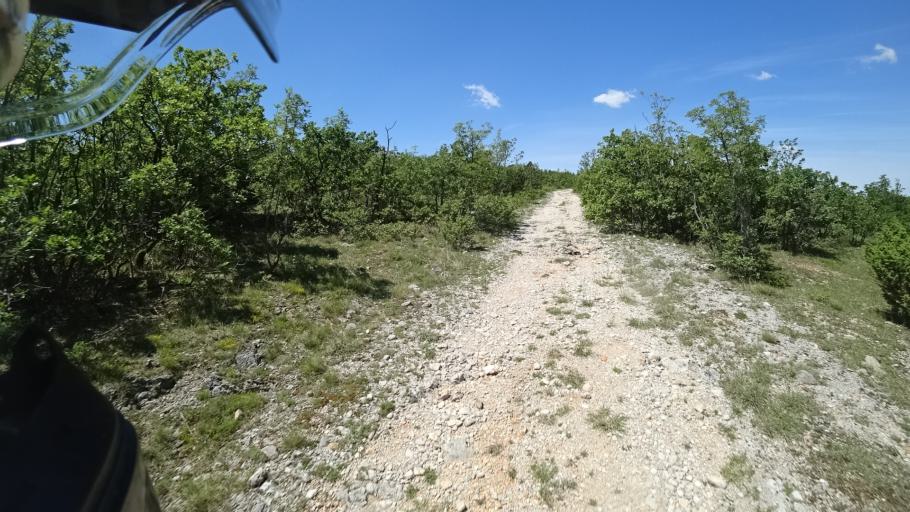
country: HR
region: Sibensko-Kniniska
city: Knin
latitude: 44.0145
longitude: 16.3299
